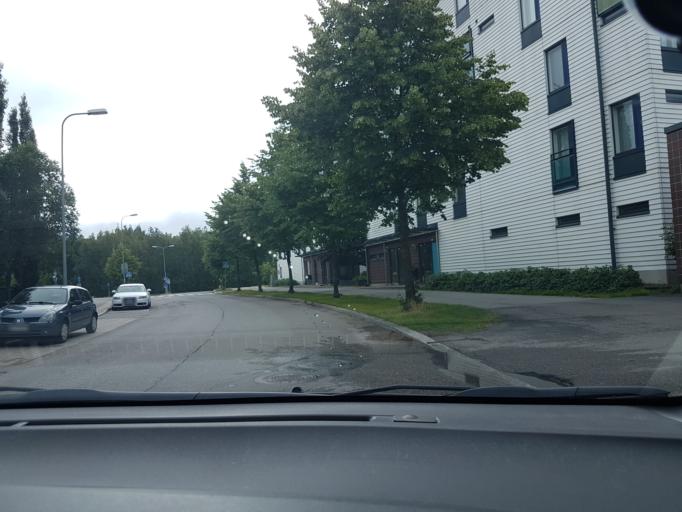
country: FI
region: Uusimaa
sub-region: Helsinki
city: Vantaa
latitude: 60.2629
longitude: 25.0390
